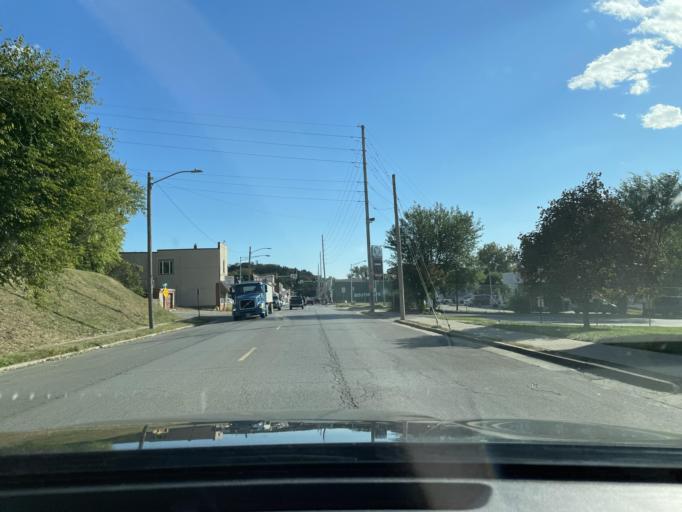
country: US
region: Kansas
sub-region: Doniphan County
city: Elwood
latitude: 39.7131
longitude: -94.8623
